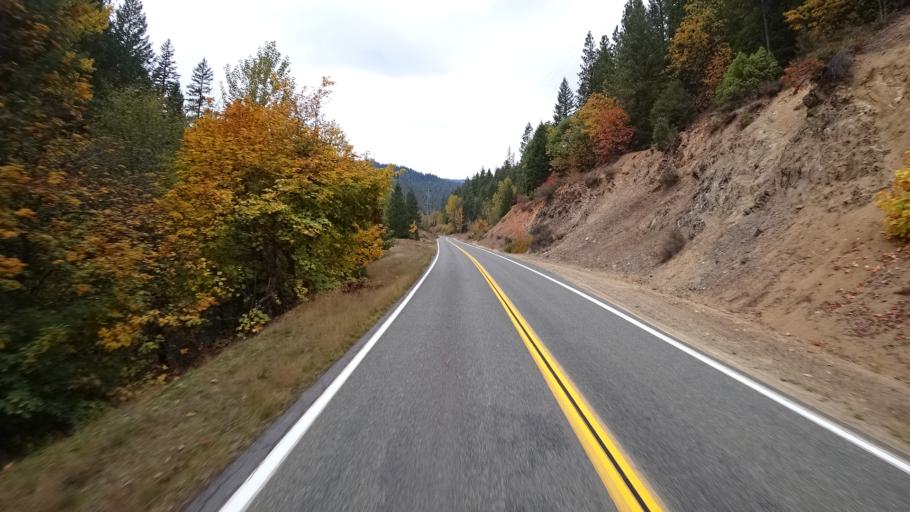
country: US
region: California
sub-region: Siskiyou County
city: Happy Camp
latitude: 41.9128
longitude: -123.4586
